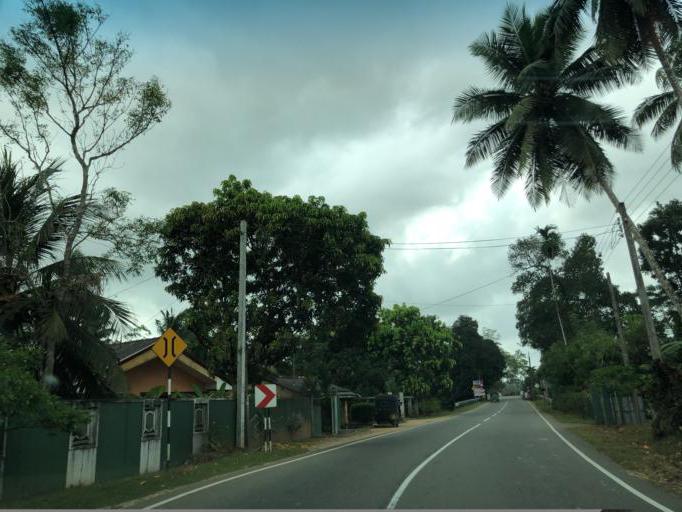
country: LK
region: Western
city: Horana South
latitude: 6.6821
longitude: 80.0935
